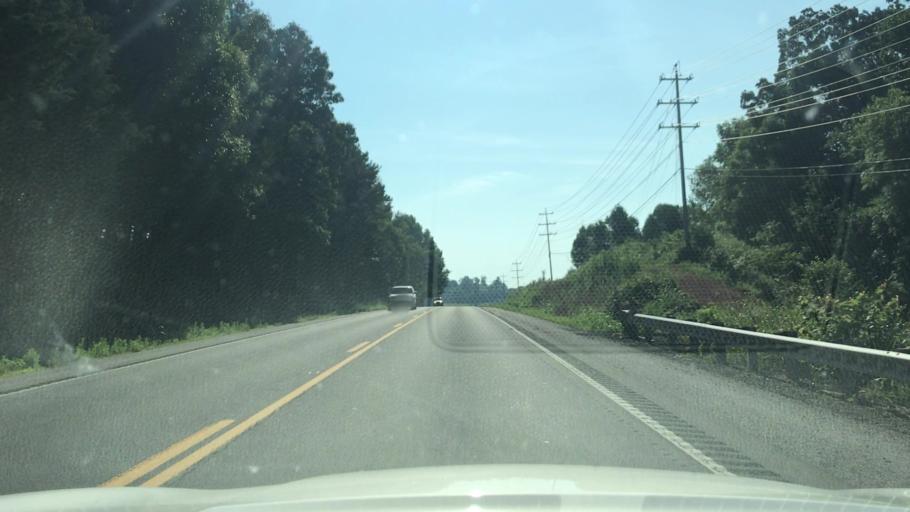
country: US
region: Tennessee
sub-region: Overton County
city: Livingston
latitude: 36.4399
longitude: -85.2538
